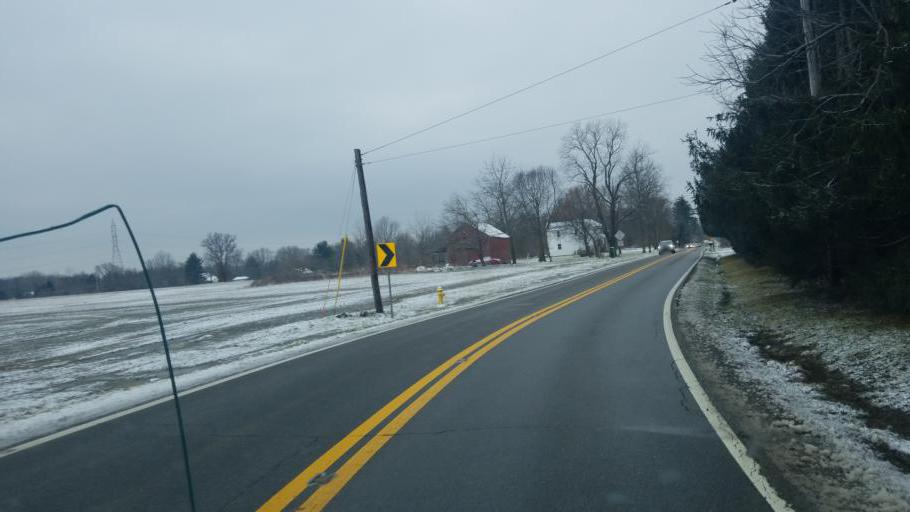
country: US
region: Ohio
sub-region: Franklin County
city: New Albany
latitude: 40.0425
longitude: -82.7841
